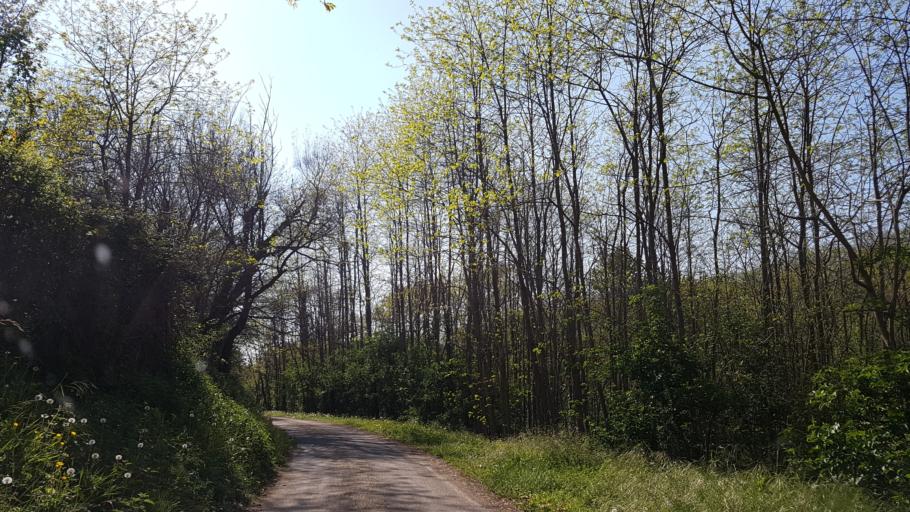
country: FR
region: Midi-Pyrenees
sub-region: Departement de l'Ariege
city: La Tour-du-Crieu
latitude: 43.0884
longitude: 1.7155
